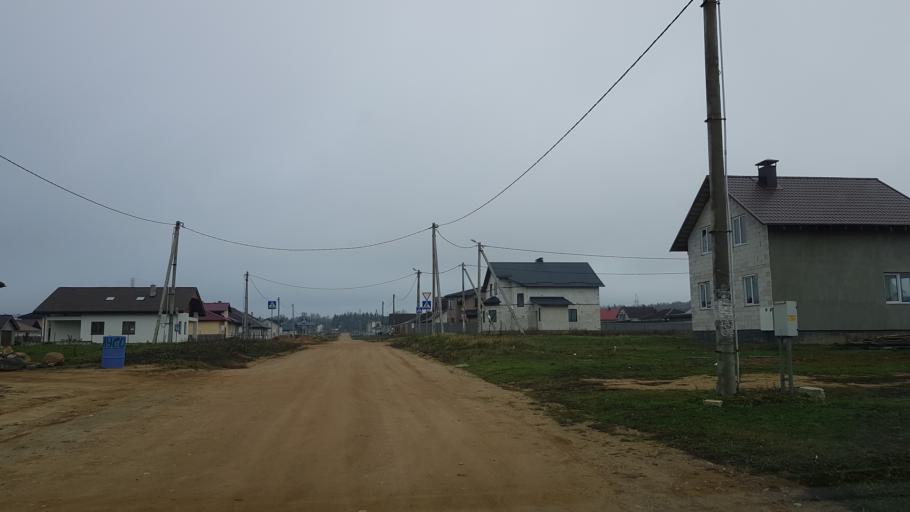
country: BY
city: Fanipol
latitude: 53.7270
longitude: 27.3250
